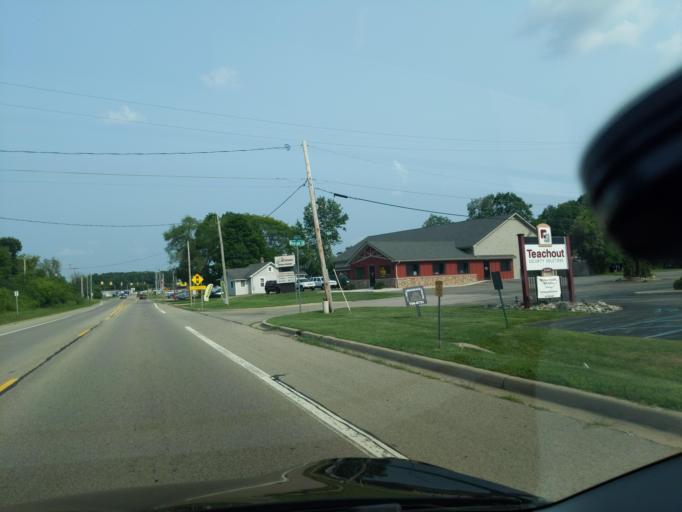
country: US
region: Michigan
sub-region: Jackson County
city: Jackson
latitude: 42.2518
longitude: -84.4504
